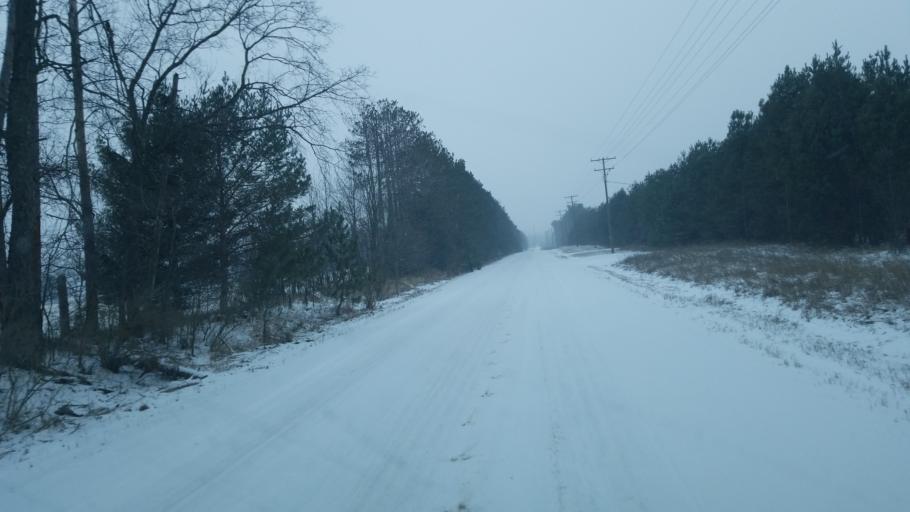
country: US
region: Michigan
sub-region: Osceola County
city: Reed City
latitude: 43.8290
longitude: -85.4154
